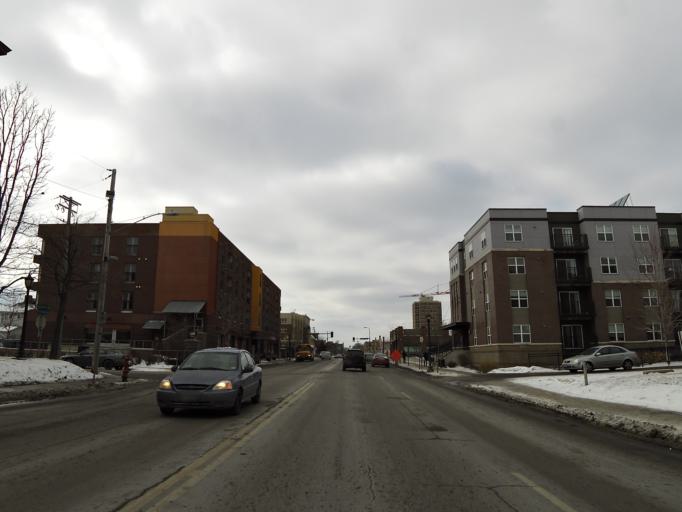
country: US
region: Minnesota
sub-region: Hennepin County
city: Minneapolis
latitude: 44.9627
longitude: -93.2661
